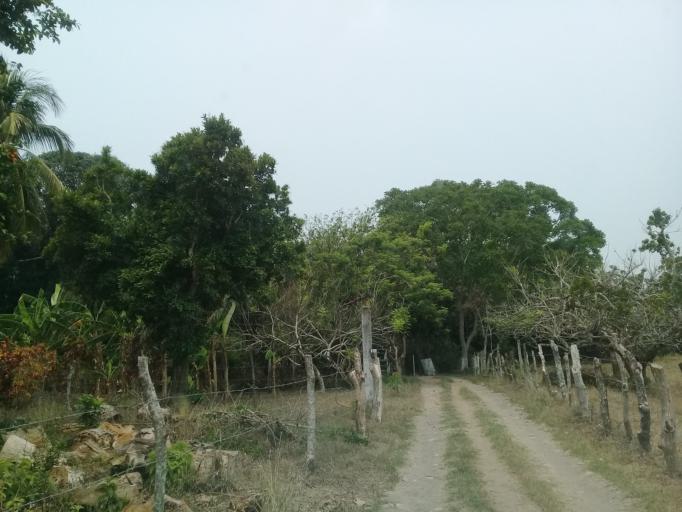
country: MX
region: Veracruz
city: Jamapa
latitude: 18.9586
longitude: -96.1965
